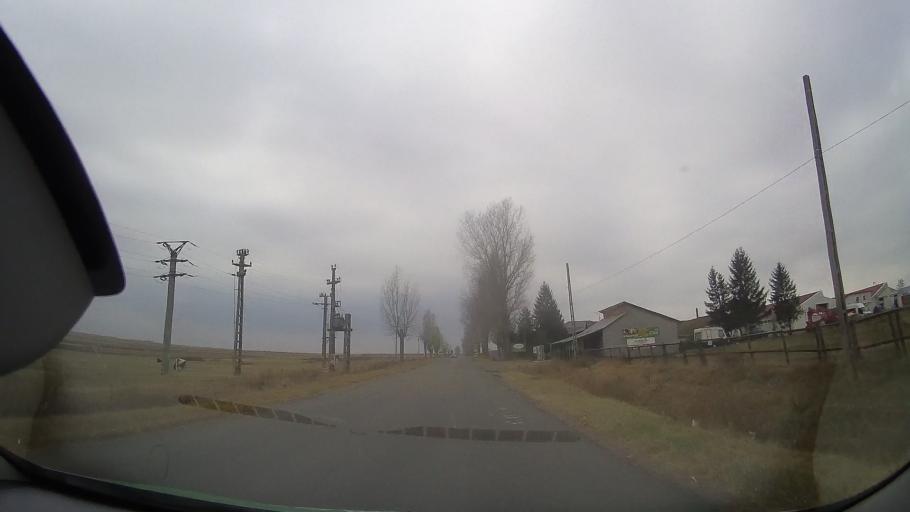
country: RO
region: Buzau
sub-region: Comuna Pogoanele
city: Pogoanele
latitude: 44.9007
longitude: 26.9759
